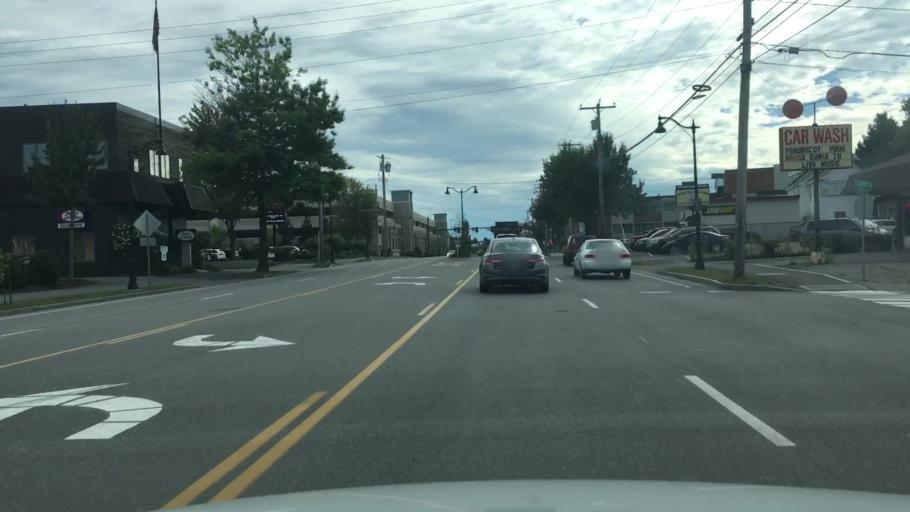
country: US
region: Maine
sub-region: Penobscot County
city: Bangor
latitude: 44.7912
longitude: -68.7766
